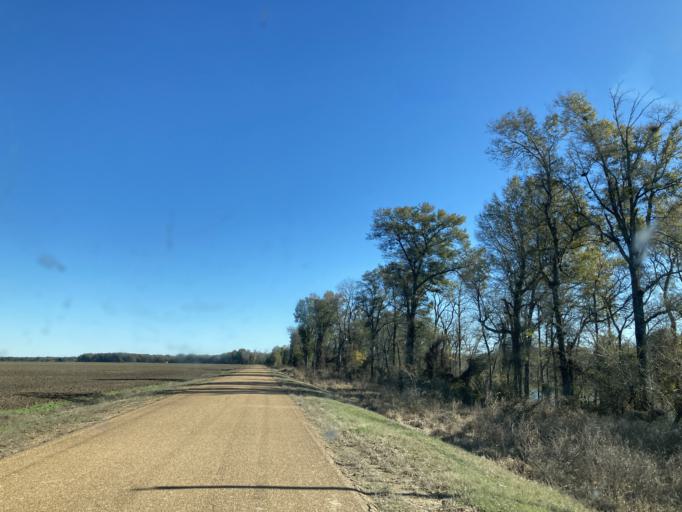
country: US
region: Mississippi
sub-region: Yazoo County
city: Yazoo City
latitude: 32.7392
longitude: -90.6343
